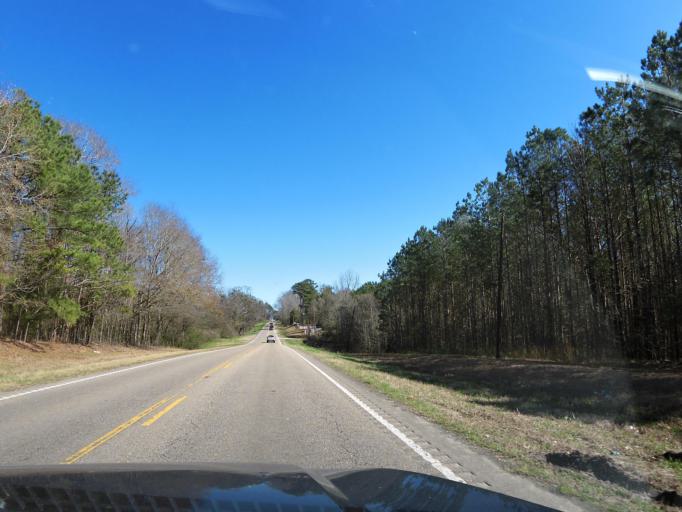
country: US
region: Alabama
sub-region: Bullock County
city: Union Springs
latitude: 32.1371
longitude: -85.7332
